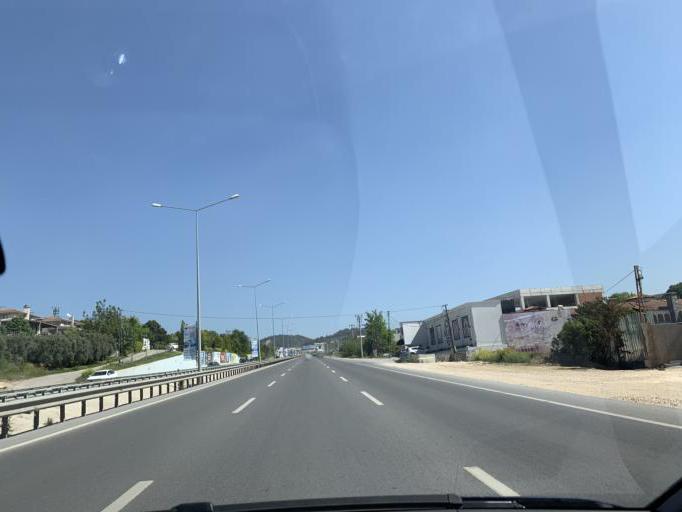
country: TR
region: Bursa
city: Niluefer
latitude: 40.2895
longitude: 28.9363
